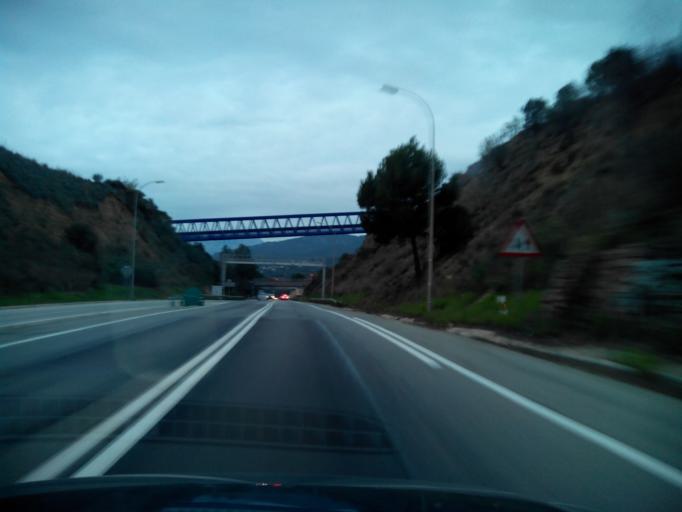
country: ES
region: Catalonia
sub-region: Provincia de Barcelona
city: Terrassa
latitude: 41.5568
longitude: 1.9857
